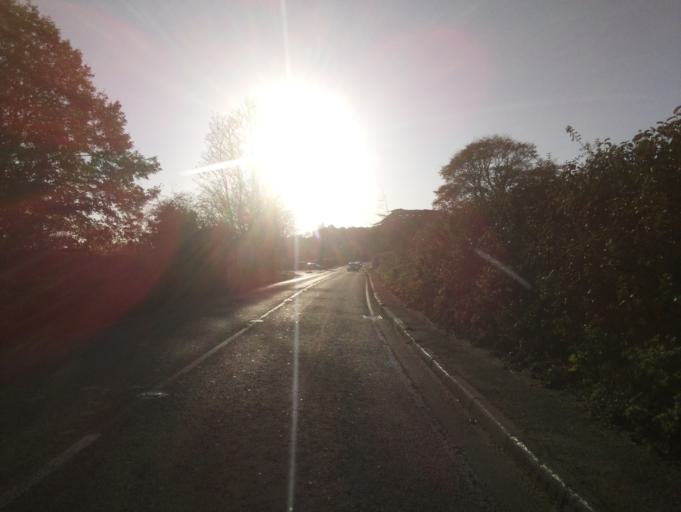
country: GB
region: England
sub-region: Dorset
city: Sherborne
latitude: 50.9572
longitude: -2.4986
